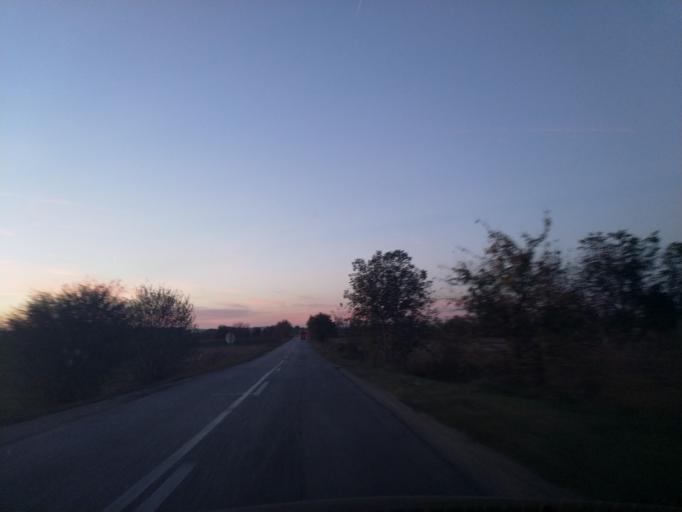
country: RS
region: Central Serbia
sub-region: Pomoravski Okrug
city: Svilajnac
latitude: 44.2296
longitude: 21.1445
